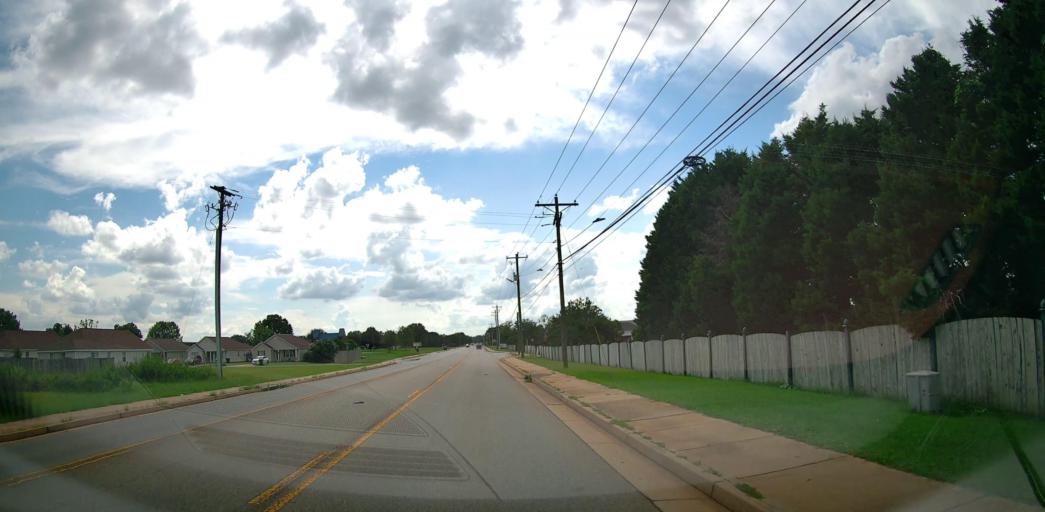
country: US
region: Georgia
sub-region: Houston County
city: Centerville
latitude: 32.5711
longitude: -83.6731
